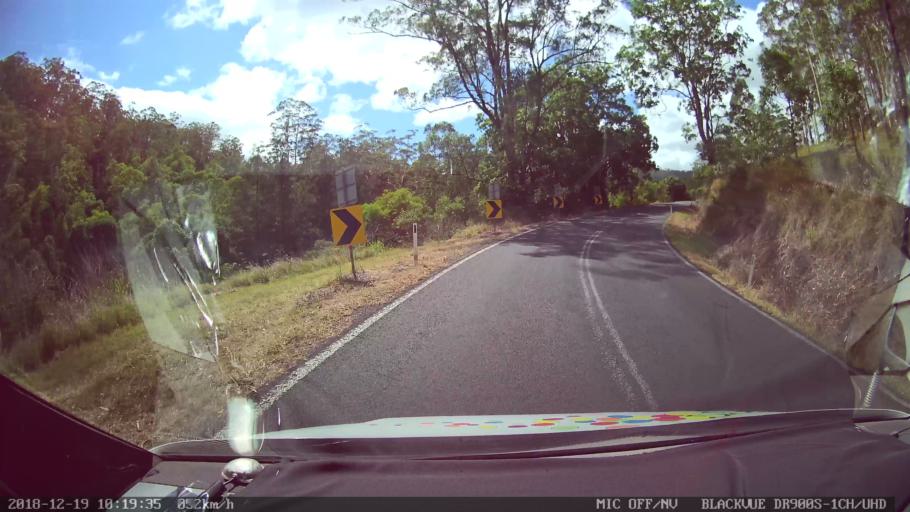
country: AU
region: New South Wales
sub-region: Kyogle
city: Kyogle
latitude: -28.5989
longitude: 153.0481
